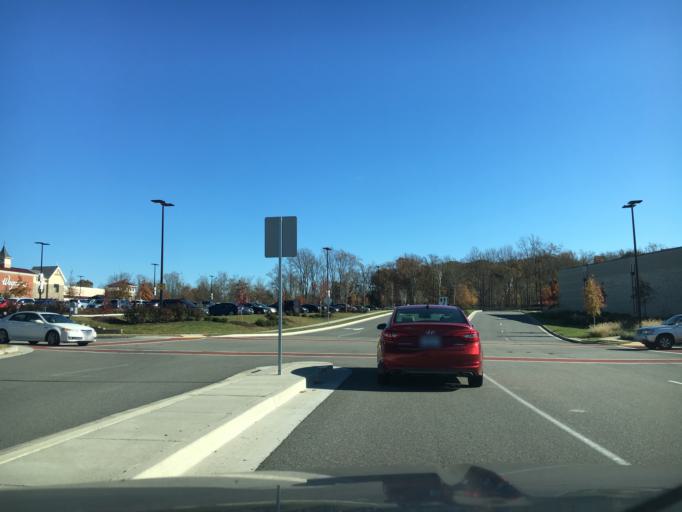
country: US
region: Virginia
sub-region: Henrico County
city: Short Pump
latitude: 37.6626
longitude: -77.6376
